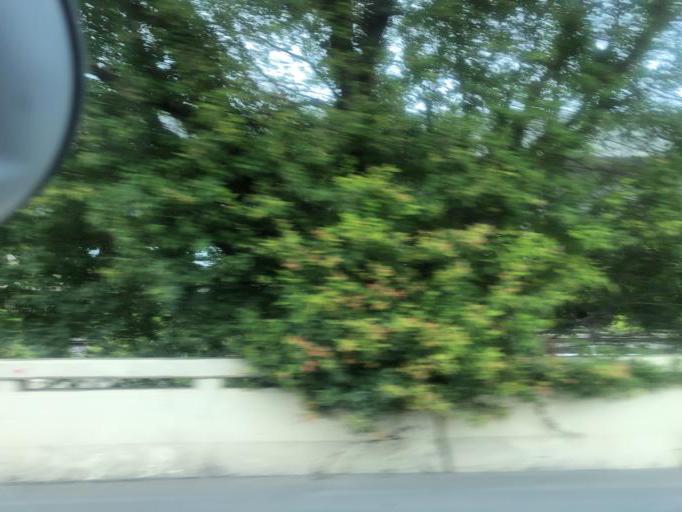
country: TH
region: Bangkok
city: Don Mueang
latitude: 13.9396
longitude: 100.6083
